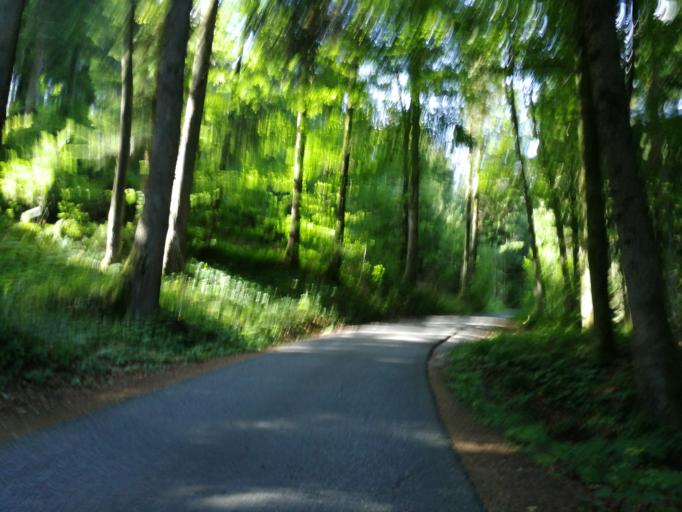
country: CH
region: Saint Gallen
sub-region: Wahlkreis See-Gaster
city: Gommiswald
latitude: 47.2537
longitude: 9.0414
